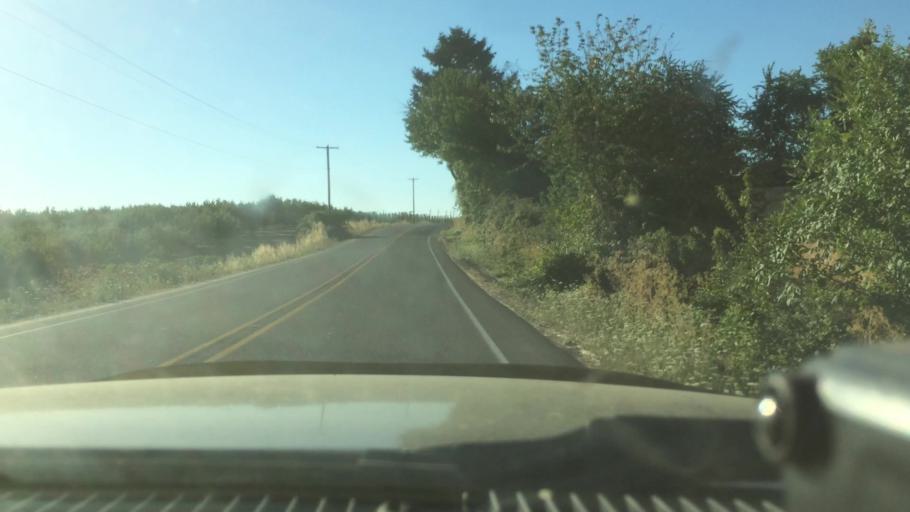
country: US
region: Oregon
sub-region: Marion County
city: Gervais
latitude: 45.1267
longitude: -122.9923
